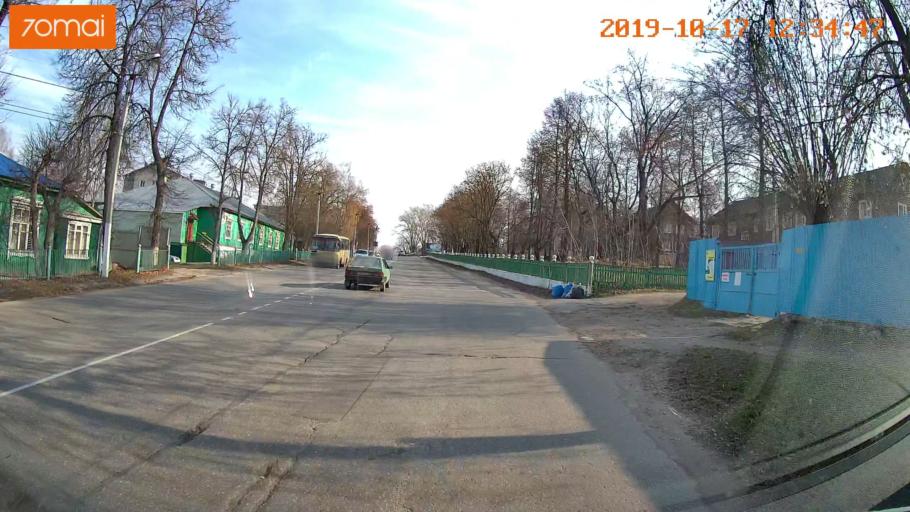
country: RU
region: Rjazan
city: Kasimov
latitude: 54.9459
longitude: 41.3677
